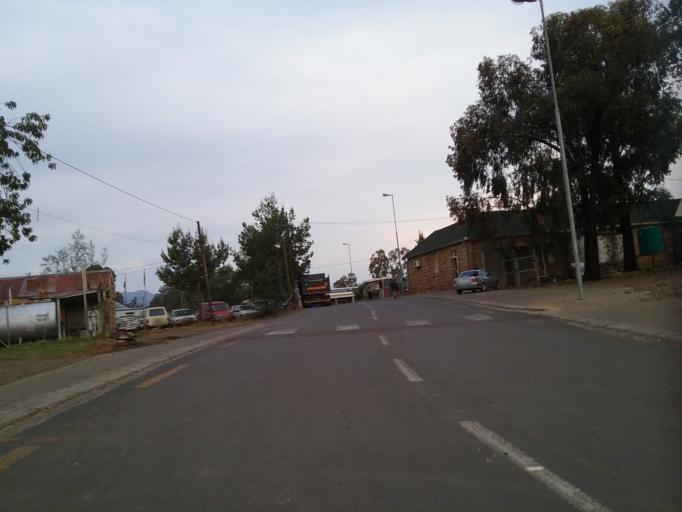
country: LS
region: Quthing
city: Quthing
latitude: -30.4070
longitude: 27.7065
